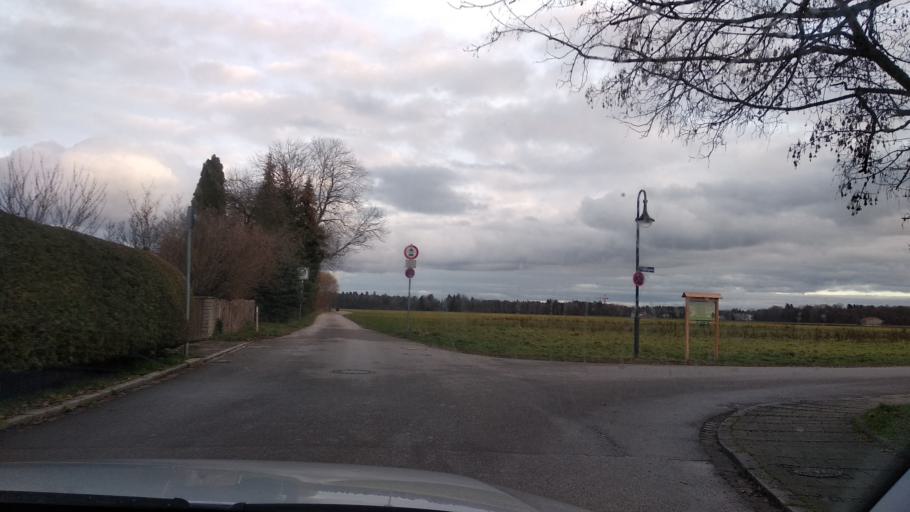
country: DE
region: Bavaria
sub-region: Upper Bavaria
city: Hohenbrunn
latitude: 48.0484
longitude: 11.7058
